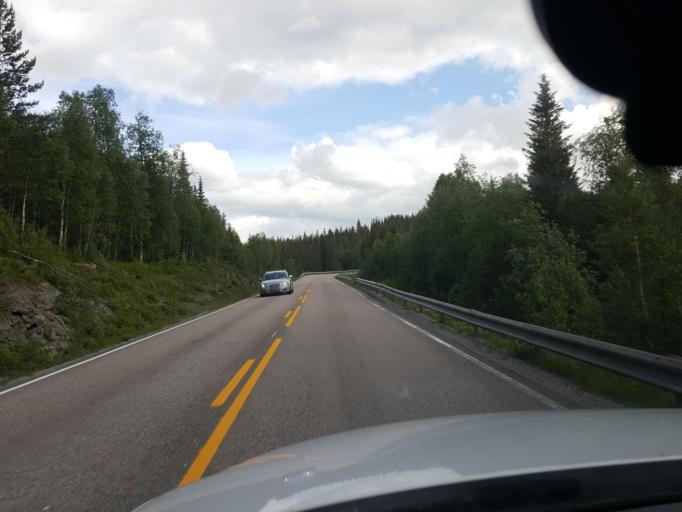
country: NO
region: Nordland
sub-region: Rana
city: Mo i Rana
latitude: 66.3126
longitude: 14.4088
